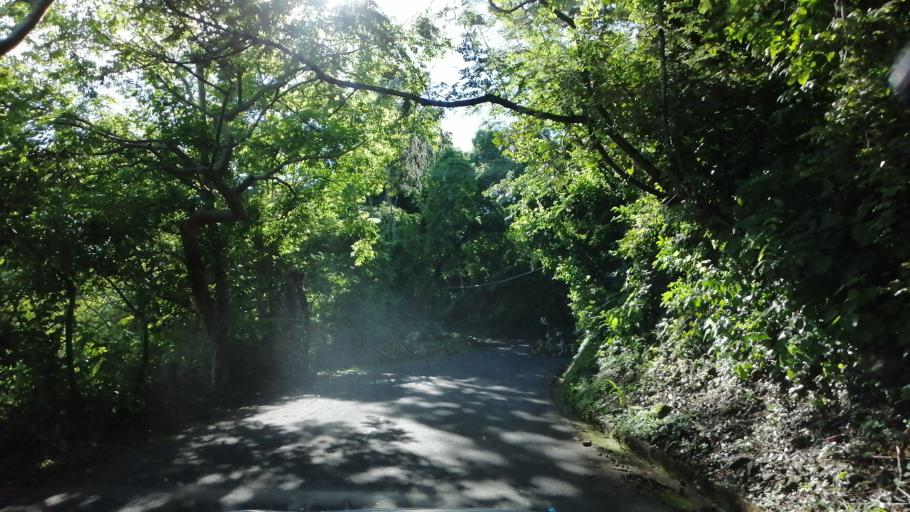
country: SV
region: Morazan
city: Cacaopera
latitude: 13.7874
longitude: -88.0291
